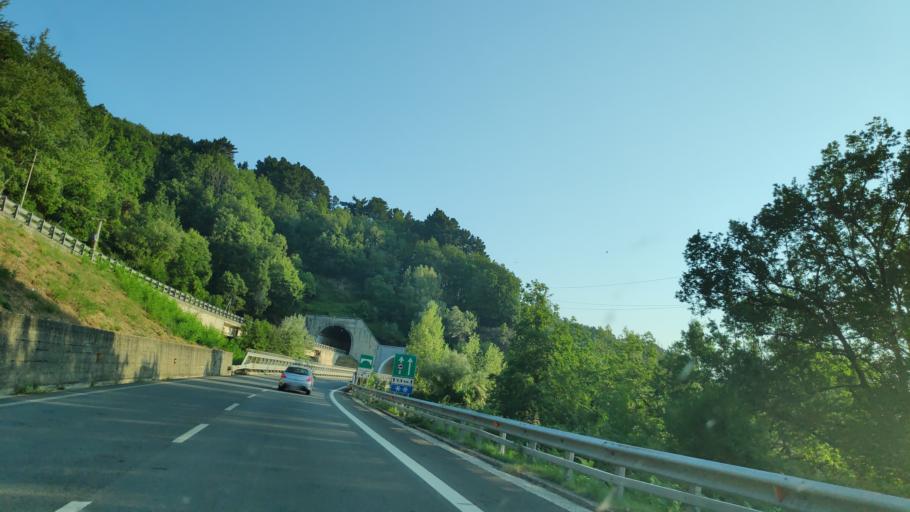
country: IT
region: Calabria
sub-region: Provincia di Cosenza
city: Belsito
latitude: 39.1739
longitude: 16.2939
